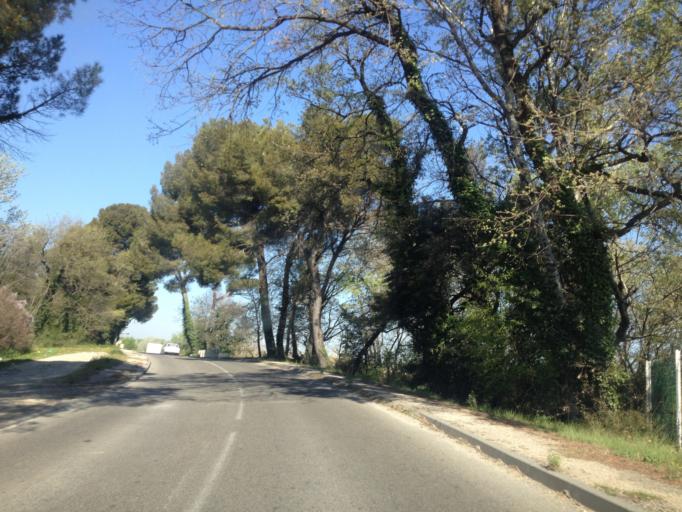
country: FR
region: Provence-Alpes-Cote d'Azur
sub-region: Departement du Vaucluse
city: Loriol-du-Comtat
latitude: 44.0763
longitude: 4.9959
